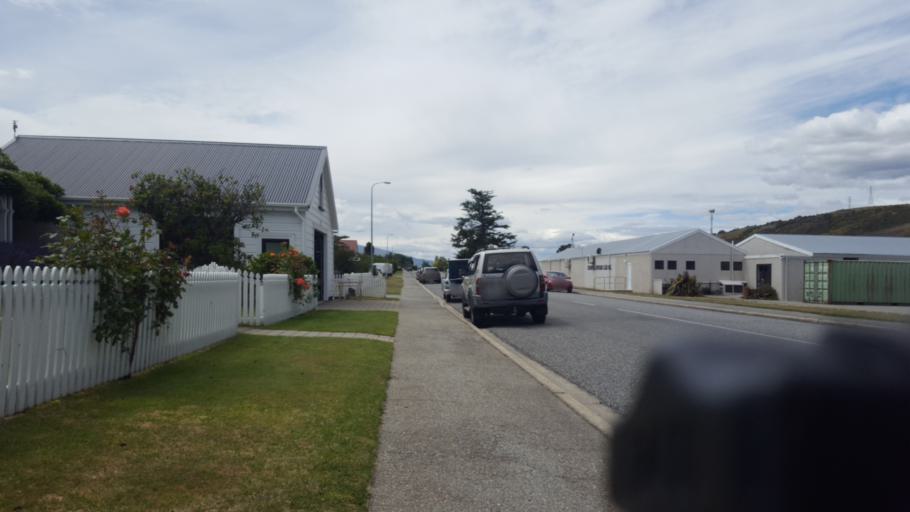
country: NZ
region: Otago
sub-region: Queenstown-Lakes District
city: Wanaka
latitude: -45.0468
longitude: 169.2122
